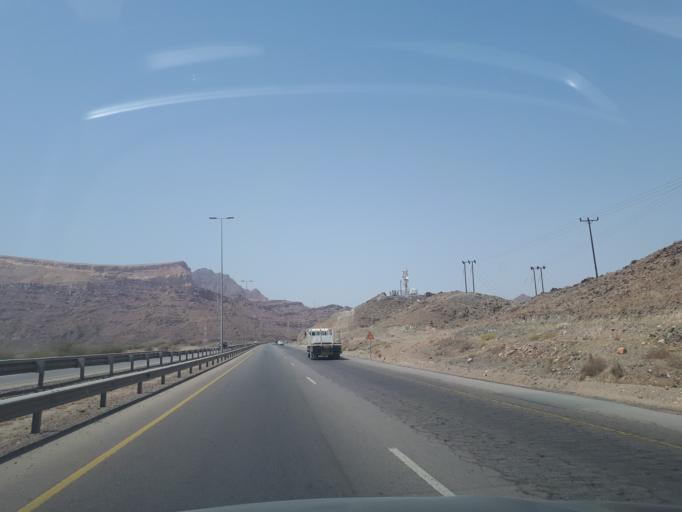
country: OM
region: Muhafazat ad Dakhiliyah
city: Bidbid
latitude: 23.4644
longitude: 58.1882
